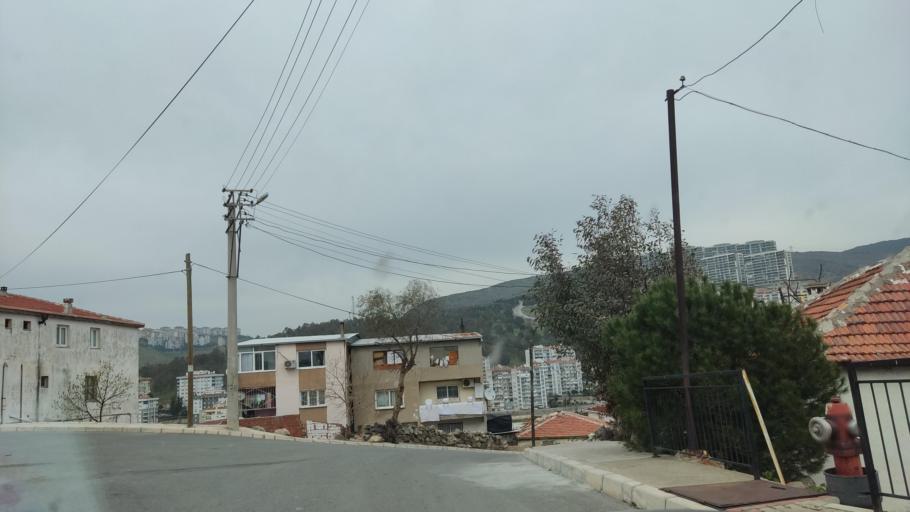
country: TR
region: Izmir
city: Karsiyaka
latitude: 38.4995
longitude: 27.0758
